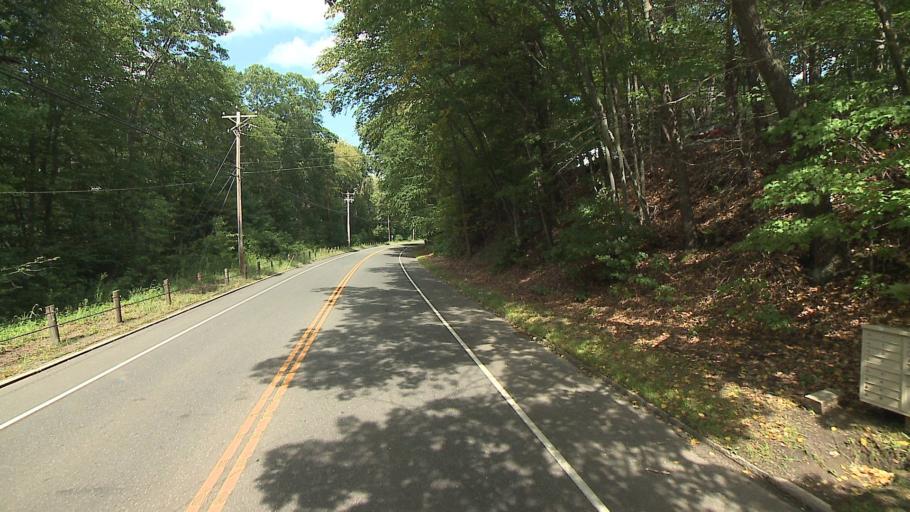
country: US
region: Connecticut
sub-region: New Haven County
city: Seymour
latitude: 41.3745
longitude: -73.0803
